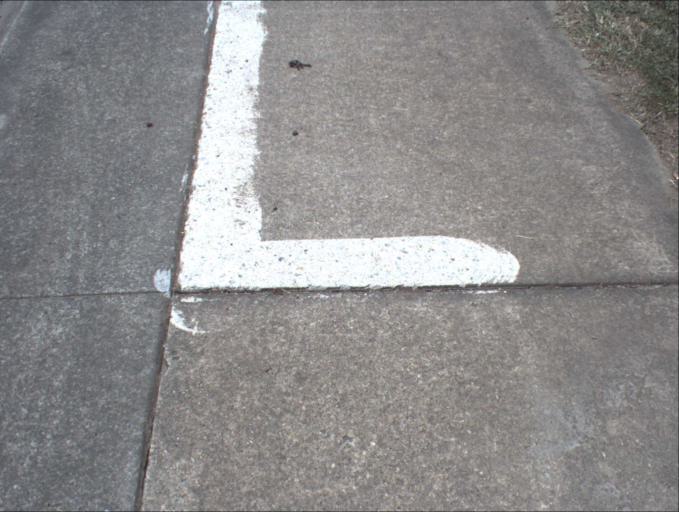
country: AU
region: Queensland
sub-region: Gold Coast
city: Yatala
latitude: -27.7260
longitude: 153.2193
